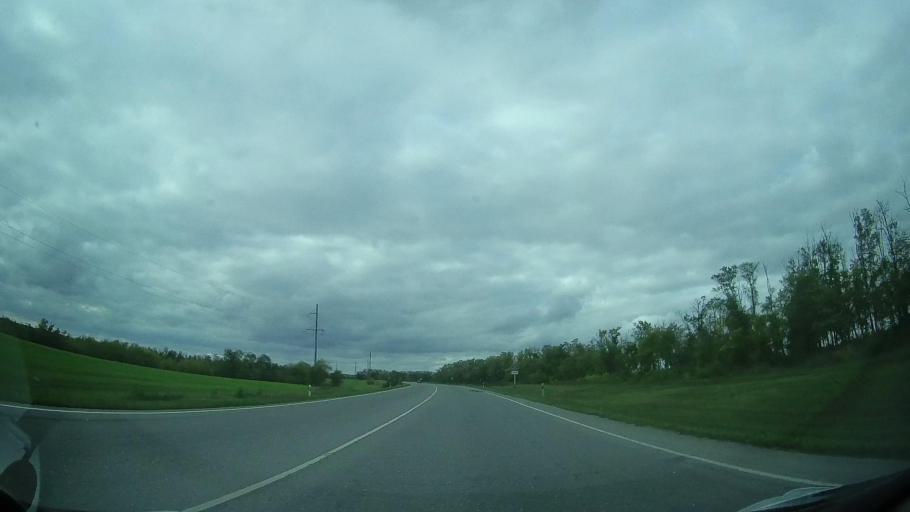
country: RU
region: Rostov
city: Mechetinskaya
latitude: 46.7845
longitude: 40.4106
